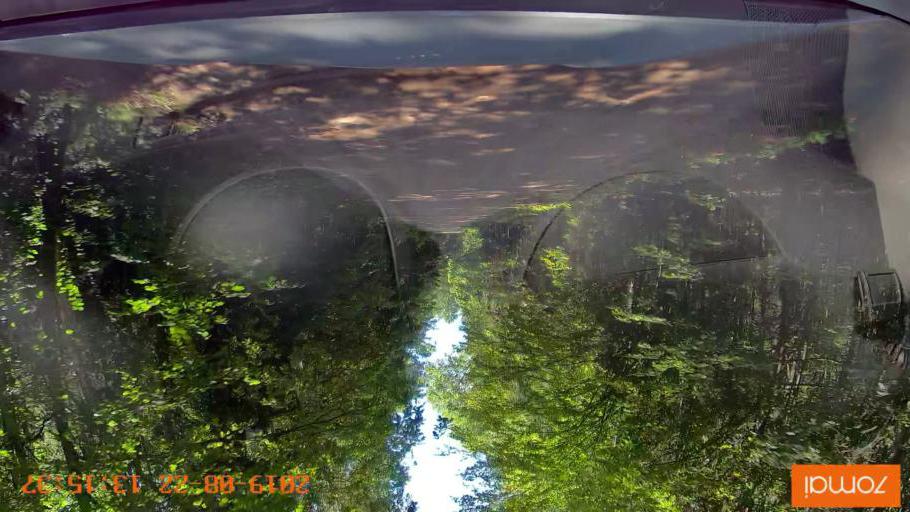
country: BY
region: Minsk
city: Prawdzinski
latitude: 53.2591
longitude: 27.8991
